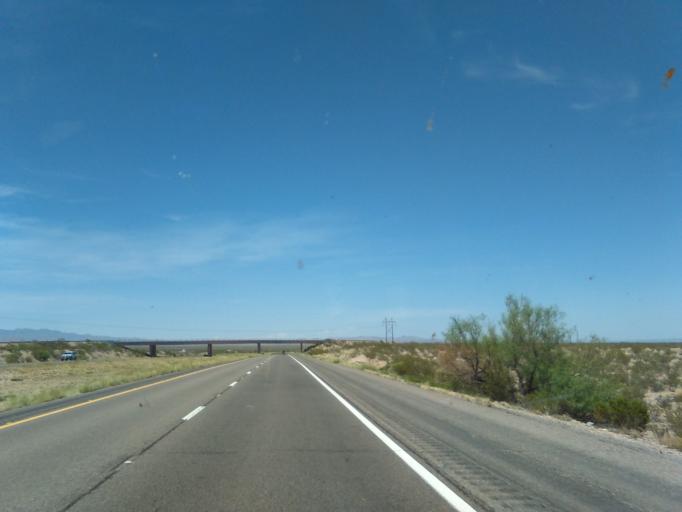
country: US
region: New Mexico
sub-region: Sierra County
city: Elephant Butte
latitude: 33.6042
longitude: -107.1536
